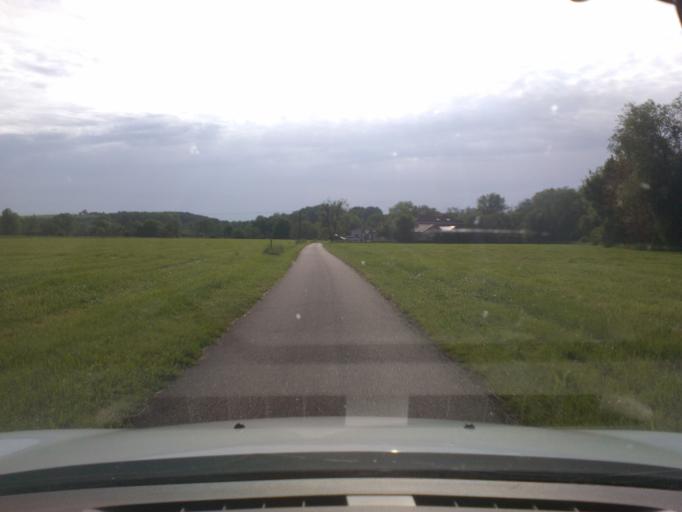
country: FR
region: Lorraine
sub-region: Departement des Vosges
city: Mirecourt
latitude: 48.3497
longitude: 6.1555
